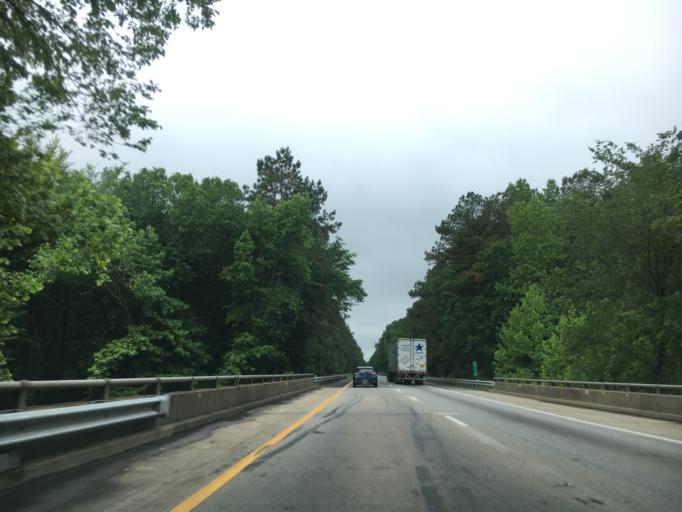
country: US
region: Virginia
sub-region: Dinwiddie County
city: Dinwiddie
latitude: 37.0616
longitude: -77.5935
